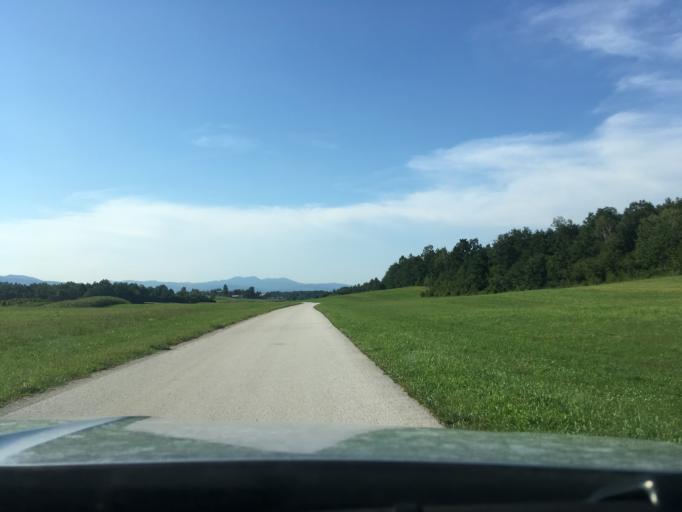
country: SI
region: Crnomelj
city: Crnomelj
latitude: 45.4619
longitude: 15.2136
